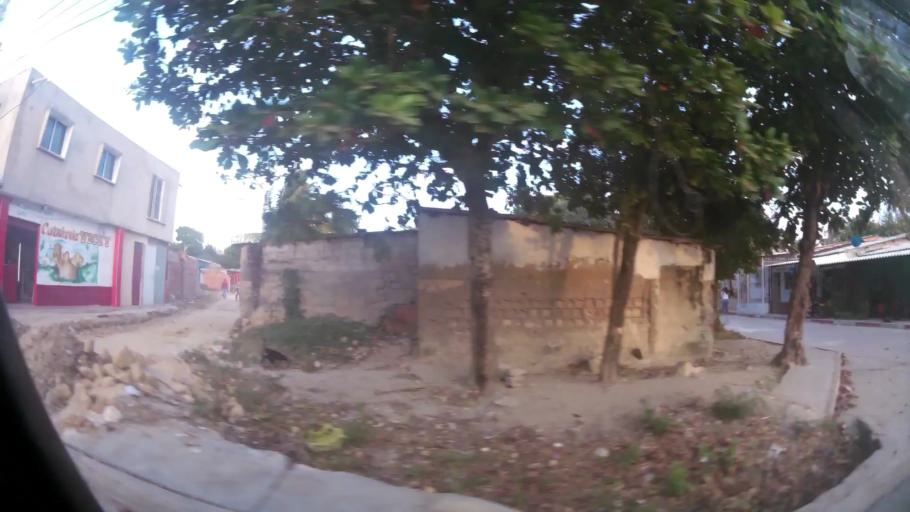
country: CO
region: Atlantico
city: Barranquilla
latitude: 10.9527
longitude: -74.8166
